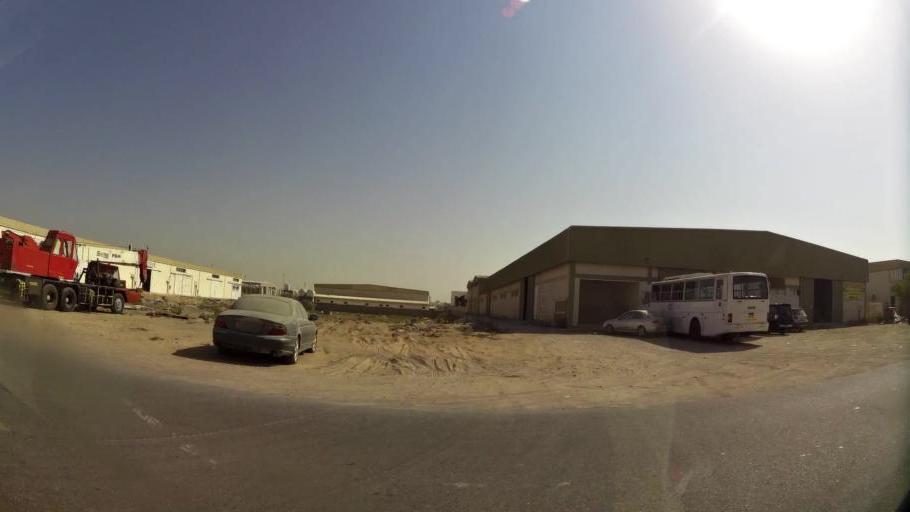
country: AE
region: Ajman
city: Ajman
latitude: 25.4294
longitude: 55.5185
